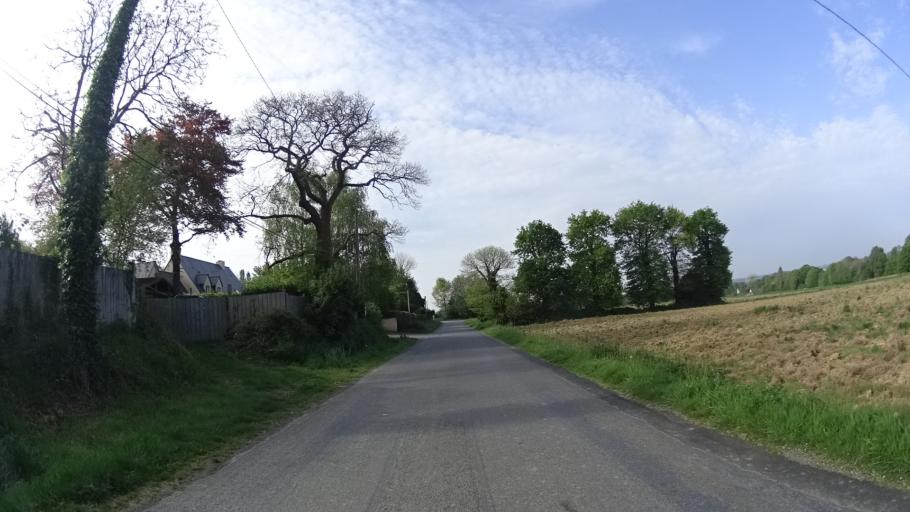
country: FR
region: Brittany
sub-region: Departement d'Ille-et-Vilaine
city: La Meziere
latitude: 48.2175
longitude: -1.7610
